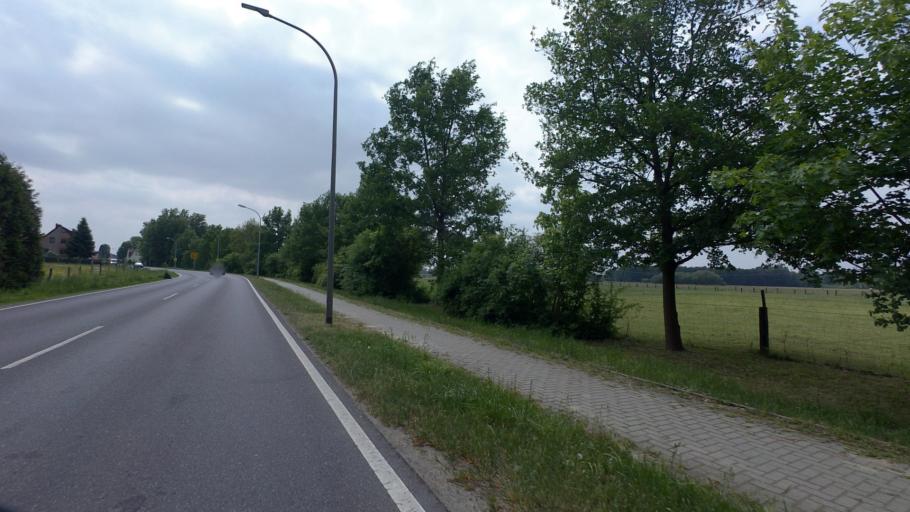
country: DE
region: Brandenburg
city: Drehnow
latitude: 51.8725
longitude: 14.3781
